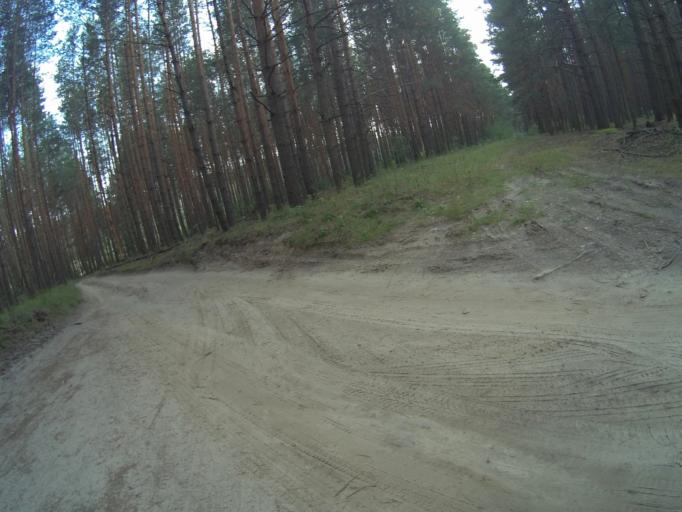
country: RU
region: Vladimir
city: Raduzhnyy
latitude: 56.0185
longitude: 40.3031
